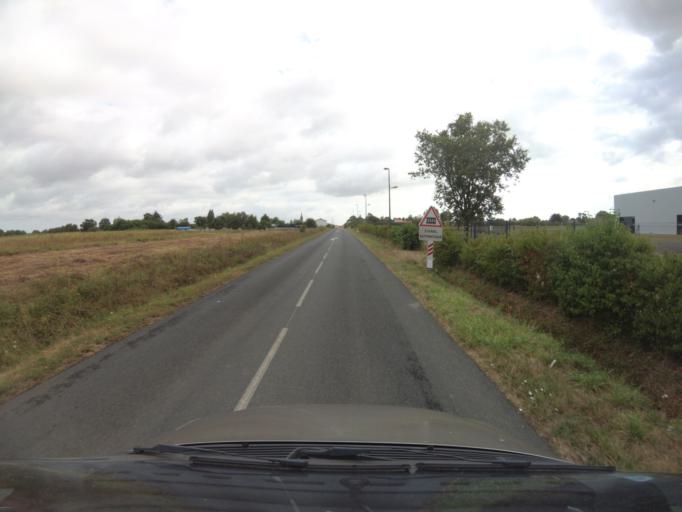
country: FR
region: Pays de la Loire
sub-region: Departement de la Vendee
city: Cugand
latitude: 47.0583
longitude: -1.2589
